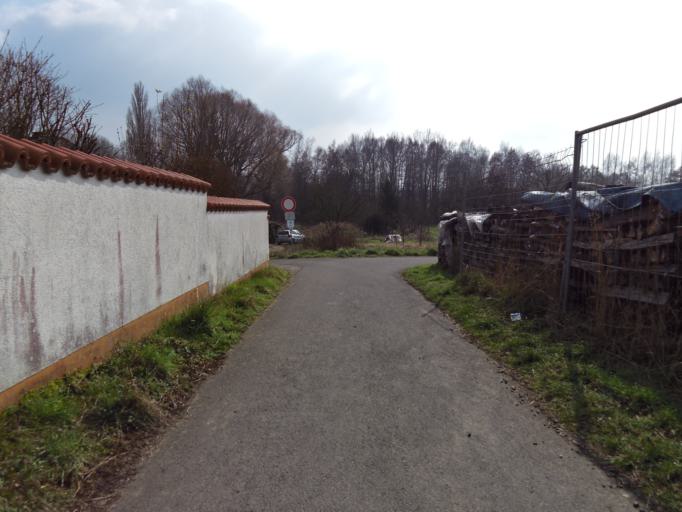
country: DE
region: Rheinland-Pfalz
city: Ebertsheim
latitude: 49.5669
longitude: 8.1035
